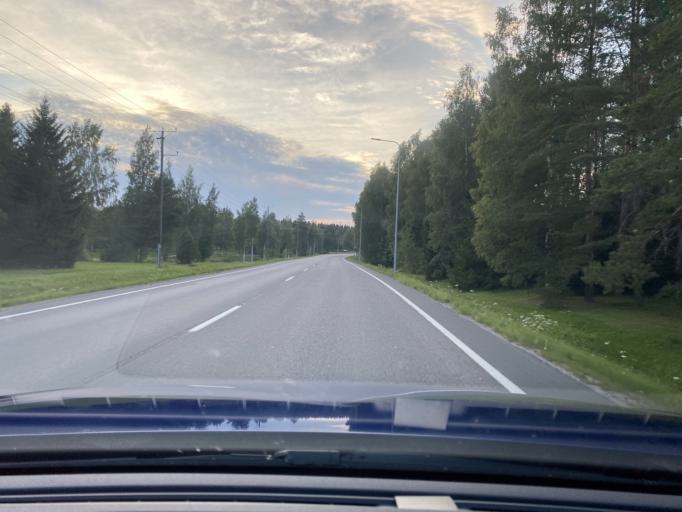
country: FI
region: Satakunta
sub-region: Pohjois-Satakunta
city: Kankaanpaeae
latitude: 61.8042
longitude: 22.3861
